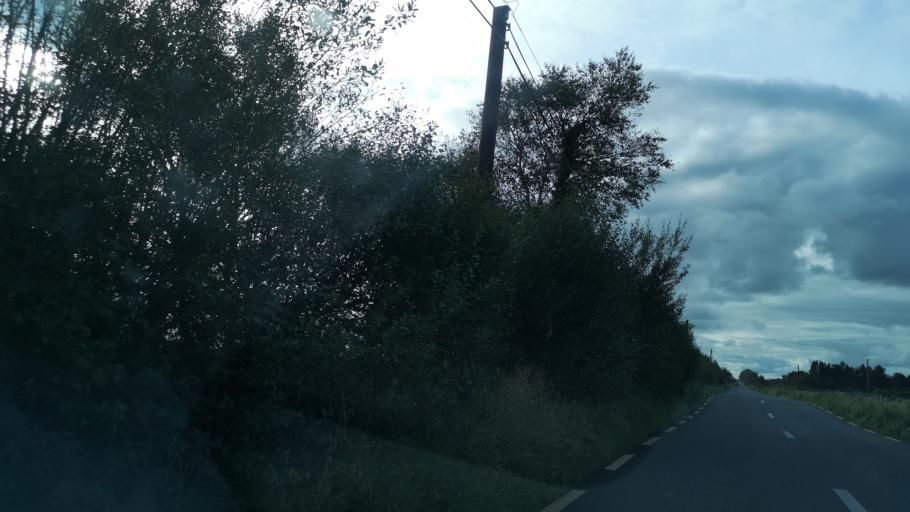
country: IE
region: Leinster
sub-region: Uibh Fhaili
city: Banagher
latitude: 53.2837
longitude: -8.0733
